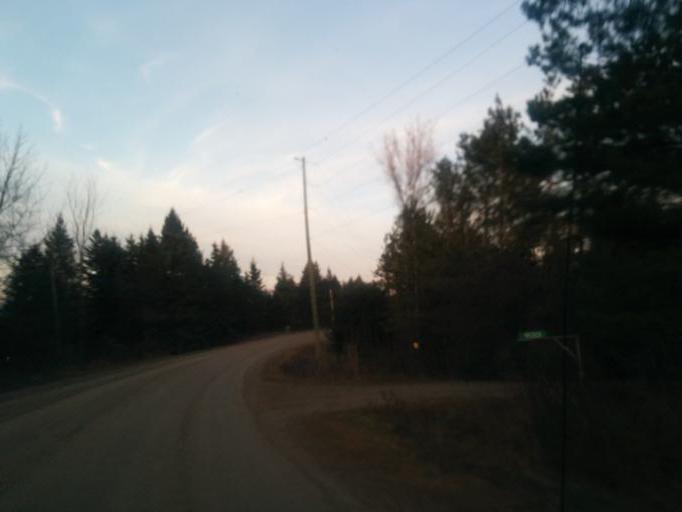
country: CA
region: Ontario
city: Orangeville
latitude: 43.9683
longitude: -79.9764
